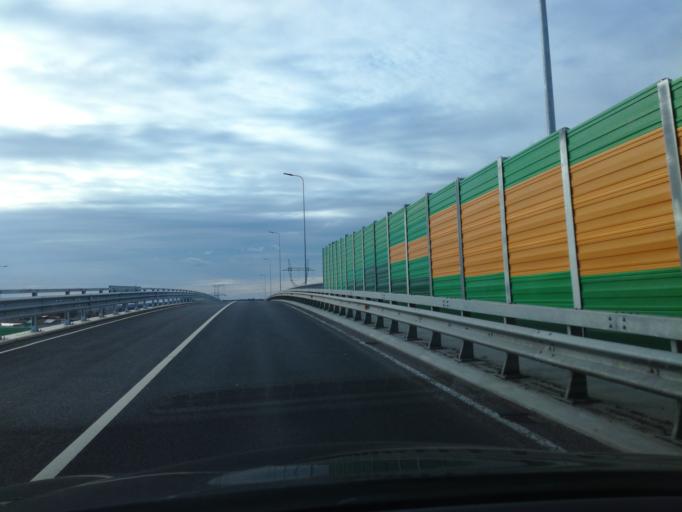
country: LT
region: Marijampoles apskritis
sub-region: Marijampole Municipality
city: Marijampole
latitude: 54.5951
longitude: 23.3950
